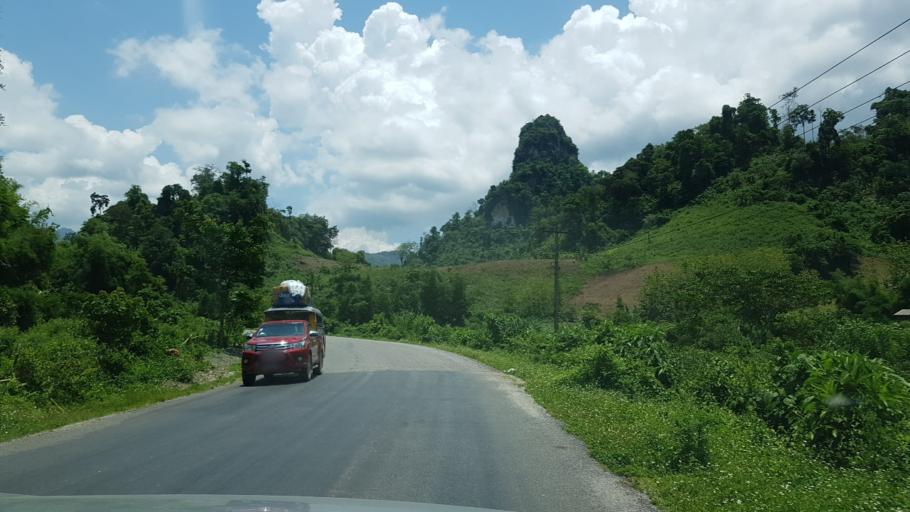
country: LA
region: Vientiane
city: Muang Kasi
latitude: 19.1236
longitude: 102.2589
